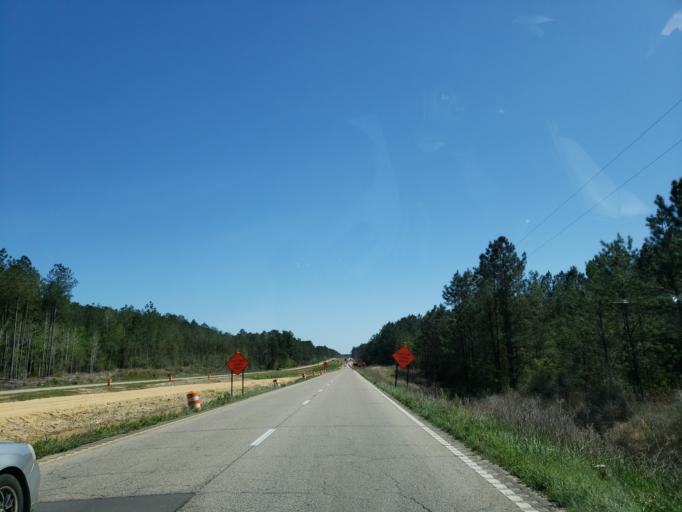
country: US
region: Mississippi
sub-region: Lamar County
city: Purvis
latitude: 31.1343
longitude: -89.2296
